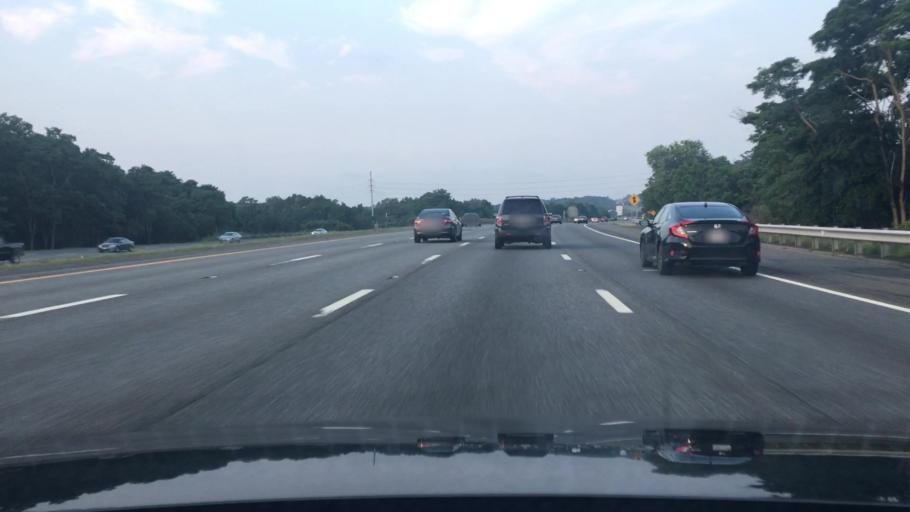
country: US
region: Massachusetts
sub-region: Essex County
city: Danvers
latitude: 42.5841
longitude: -70.9626
